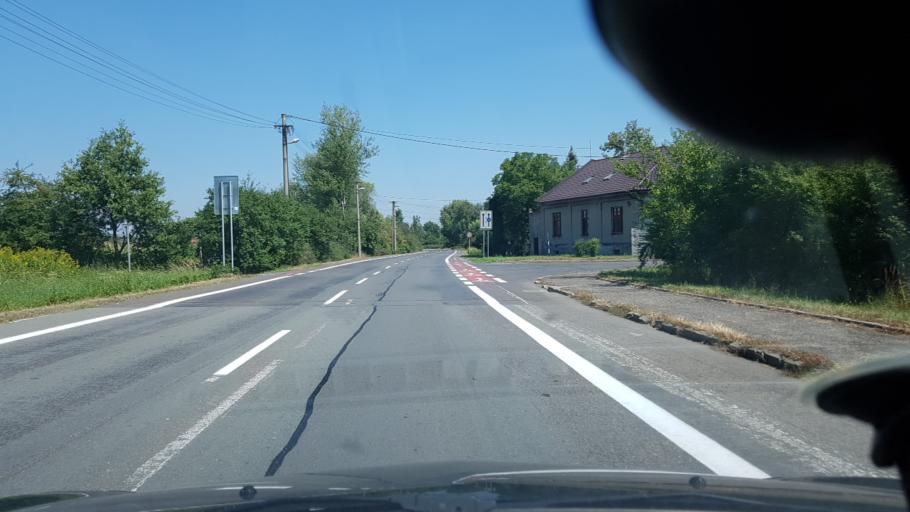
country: CZ
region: Moravskoslezsky
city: Stary Bohumin
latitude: 49.8980
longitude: 18.3334
